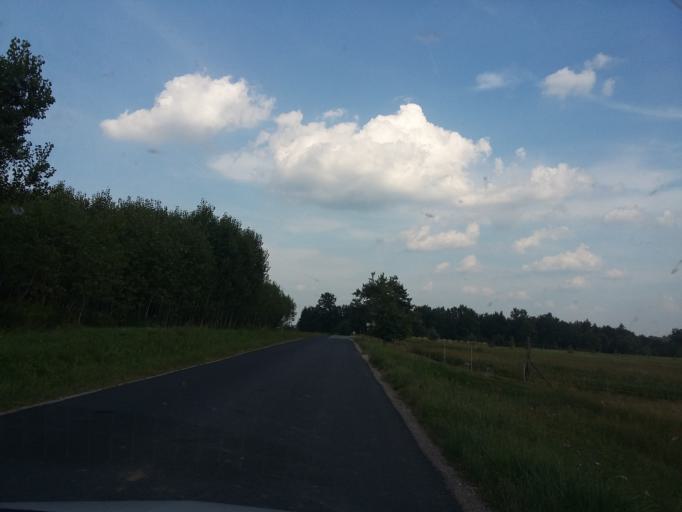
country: SI
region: Hodos-Hodos
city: Hodos
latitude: 46.8500
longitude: 16.3942
